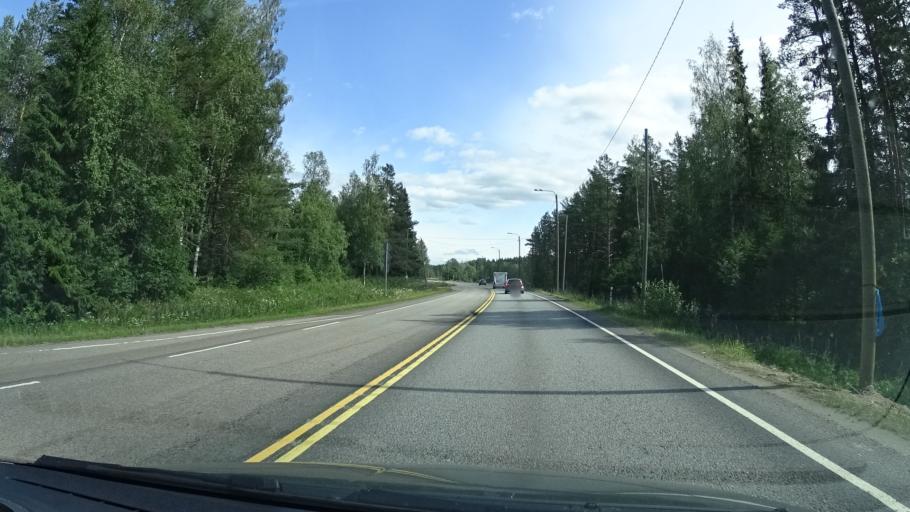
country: FI
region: Central Finland
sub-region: Jyvaeskylae
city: Muurame
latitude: 62.2672
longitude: 25.5261
